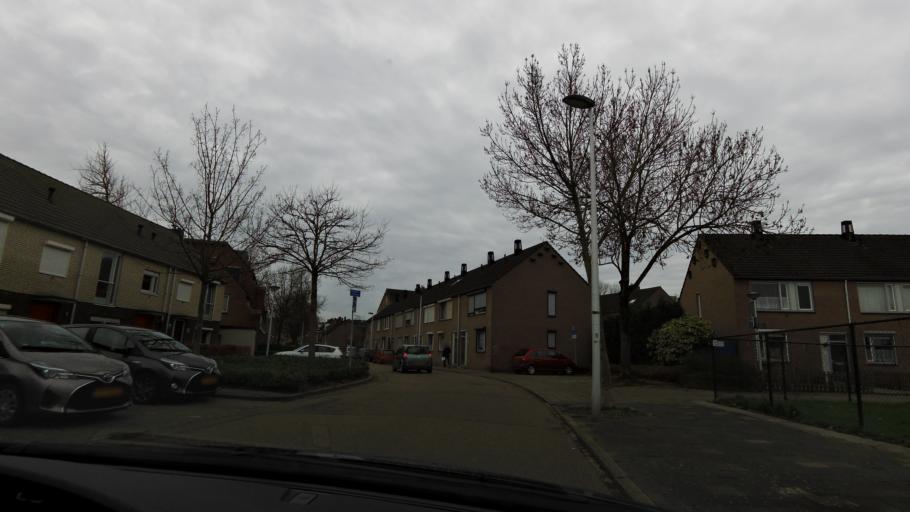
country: NL
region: Limburg
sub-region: Gemeente Maastricht
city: Maastricht
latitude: 50.8533
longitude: 5.7083
